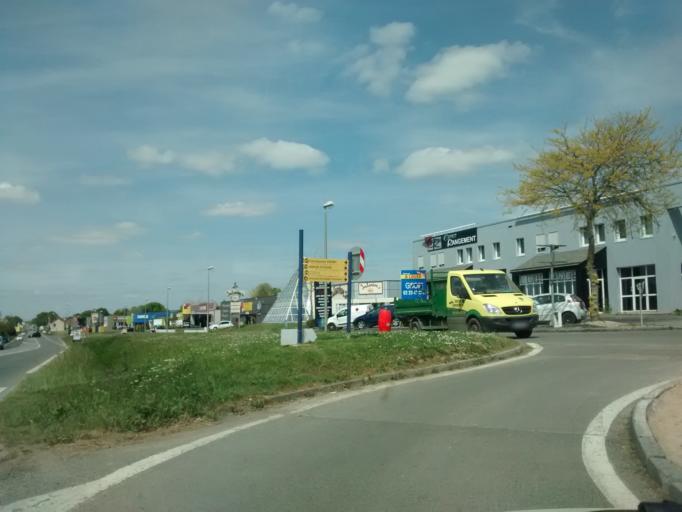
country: FR
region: Brittany
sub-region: Departement d'Ille-et-Vilaine
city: La Chapelle-des-Fougeretz
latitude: 48.1841
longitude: -1.7244
